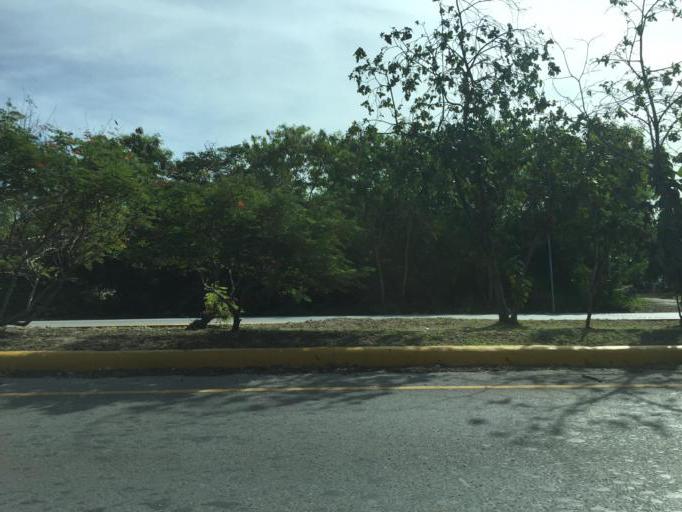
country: DO
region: San Juan
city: Punta Cana
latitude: 18.5600
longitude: -68.3742
